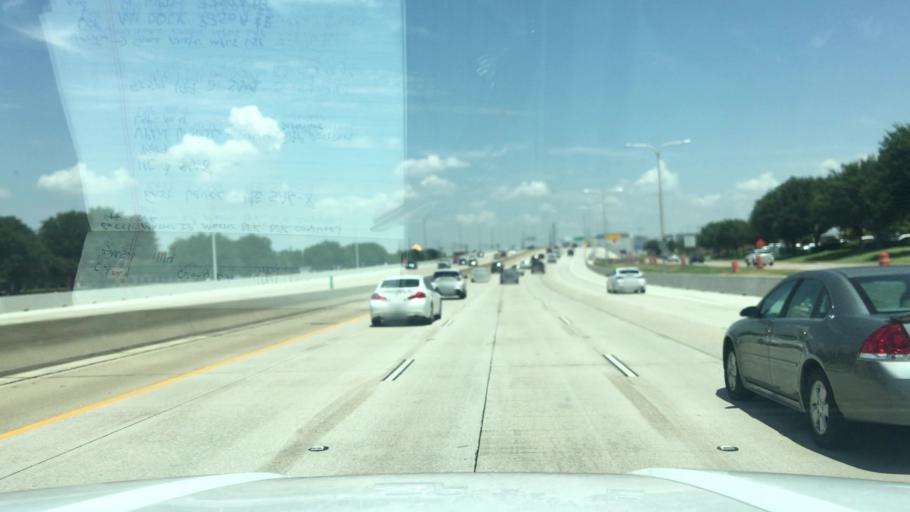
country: US
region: Texas
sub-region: Denton County
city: The Colony
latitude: 33.0499
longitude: -96.8295
